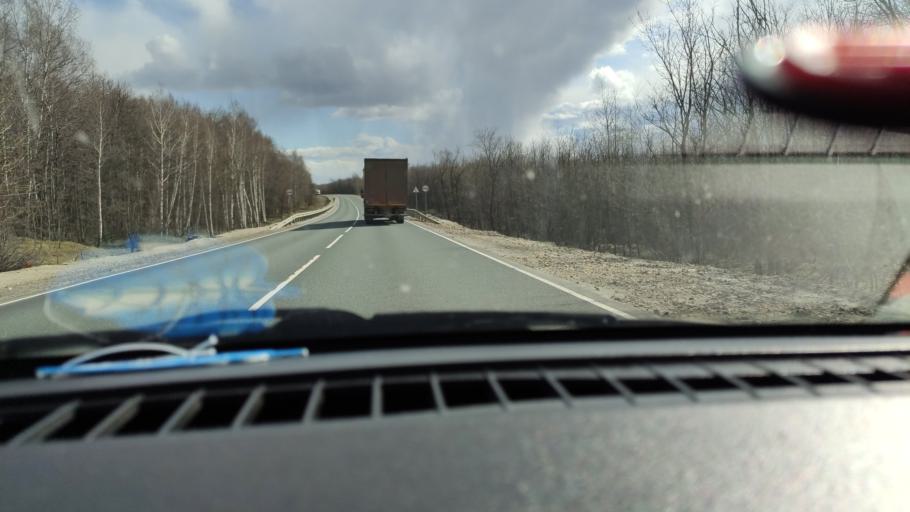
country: RU
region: Saratov
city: Khvalynsk
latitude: 52.4772
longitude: 48.0134
